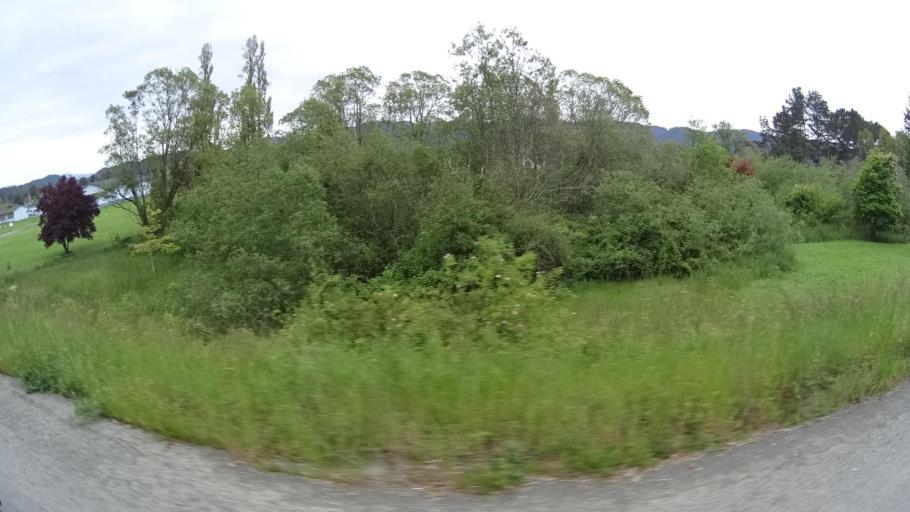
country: US
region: California
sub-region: Humboldt County
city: Blue Lake
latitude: 40.8862
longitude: -123.9939
